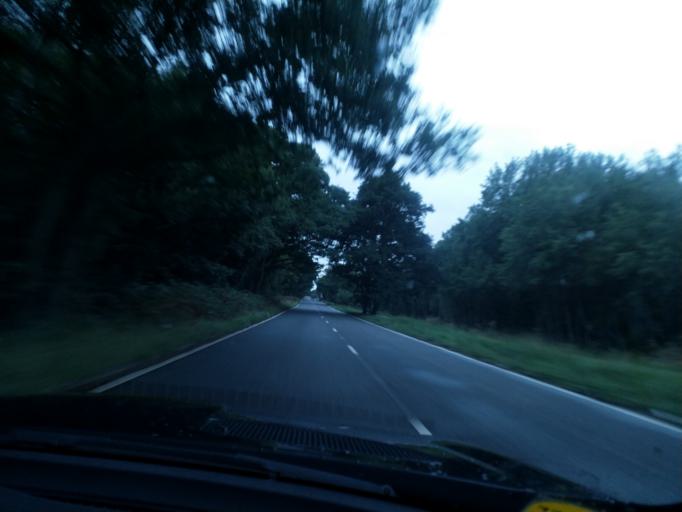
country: GB
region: England
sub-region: Bracknell Forest
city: Sandhurst
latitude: 51.3287
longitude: -0.7910
